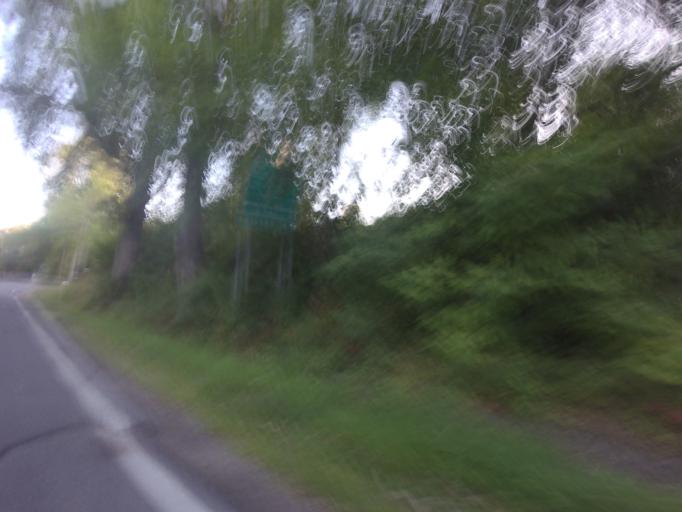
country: CA
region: Quebec
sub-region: Laurentides
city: Oka
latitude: 45.4502
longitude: -74.1104
